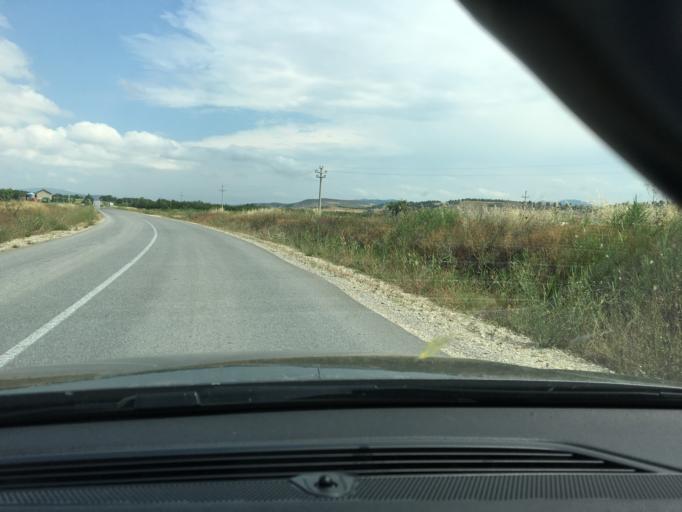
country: MK
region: Sveti Nikole
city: Sveti Nikole
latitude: 41.8799
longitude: 21.9399
